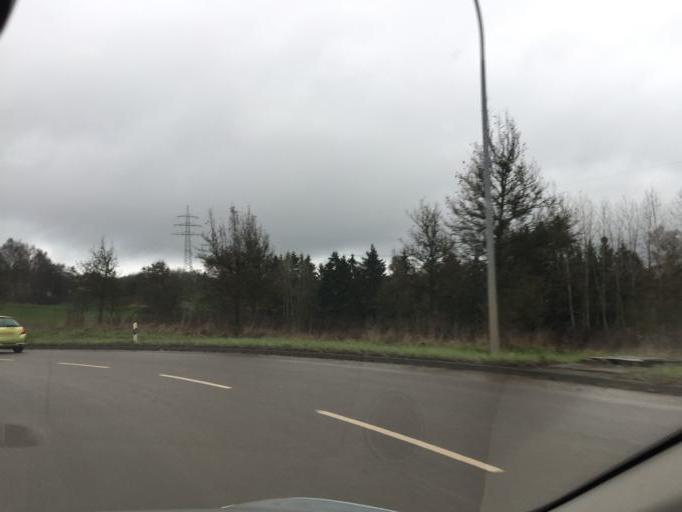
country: LU
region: Diekirch
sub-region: Canton de Diekirch
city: Diekirch
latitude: 49.8860
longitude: 6.1374
